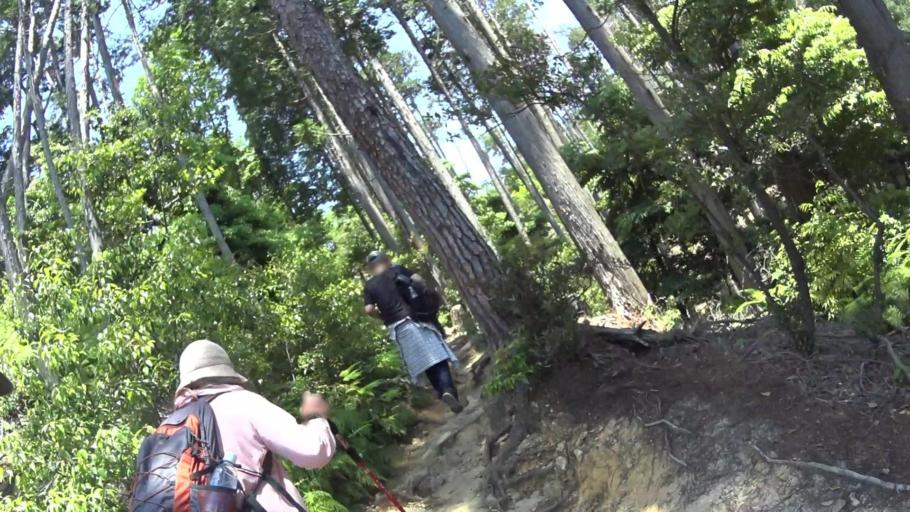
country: JP
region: Shiga Prefecture
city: Otsu-shi
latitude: 35.0133
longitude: 135.8131
